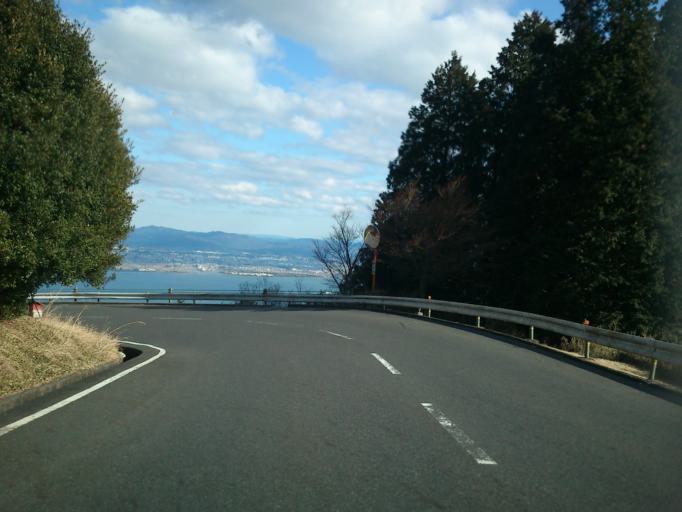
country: JP
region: Shiga Prefecture
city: Otsu-shi
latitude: 35.0511
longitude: 135.8371
